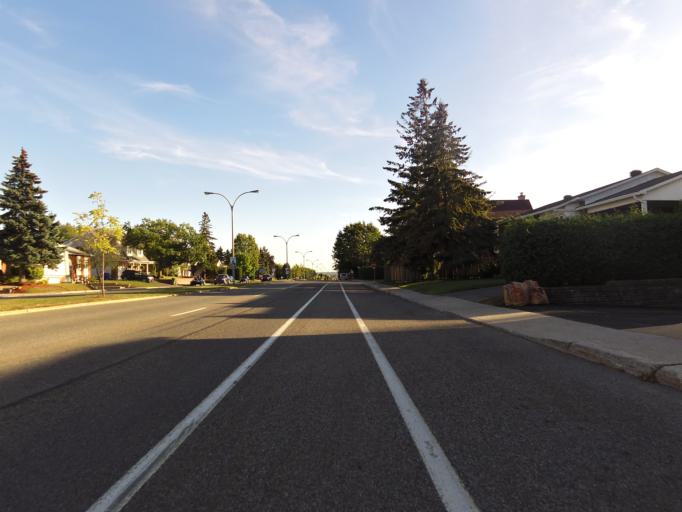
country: CA
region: Ontario
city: Bells Corners
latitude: 45.4071
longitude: -75.8386
